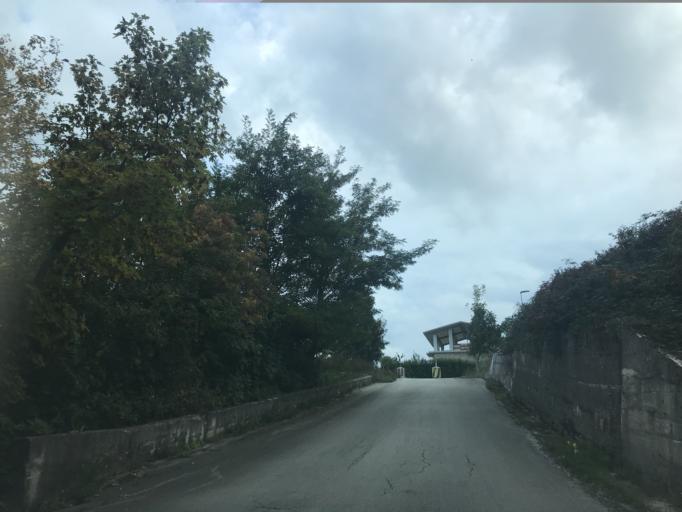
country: IT
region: Molise
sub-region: Provincia di Campobasso
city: Duronia
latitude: 41.6607
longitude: 14.4612
